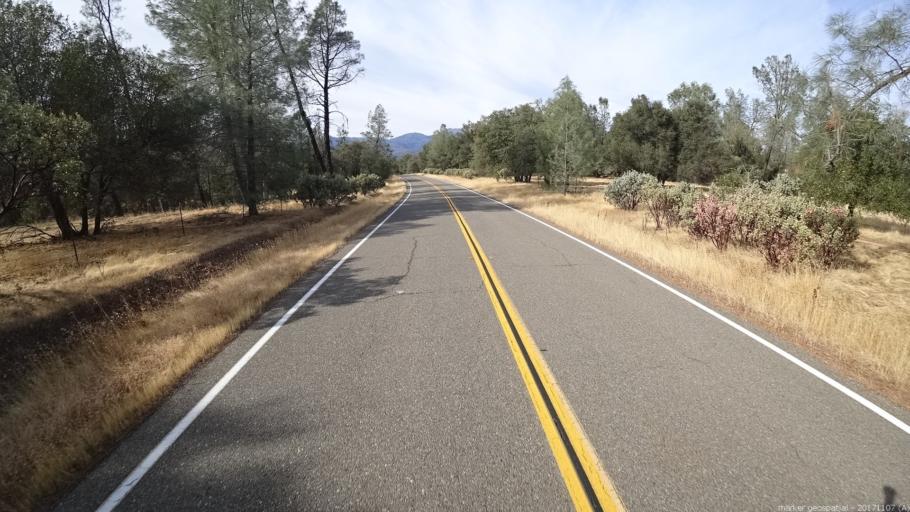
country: US
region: California
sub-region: Shasta County
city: Shasta
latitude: 40.4998
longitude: -122.5203
